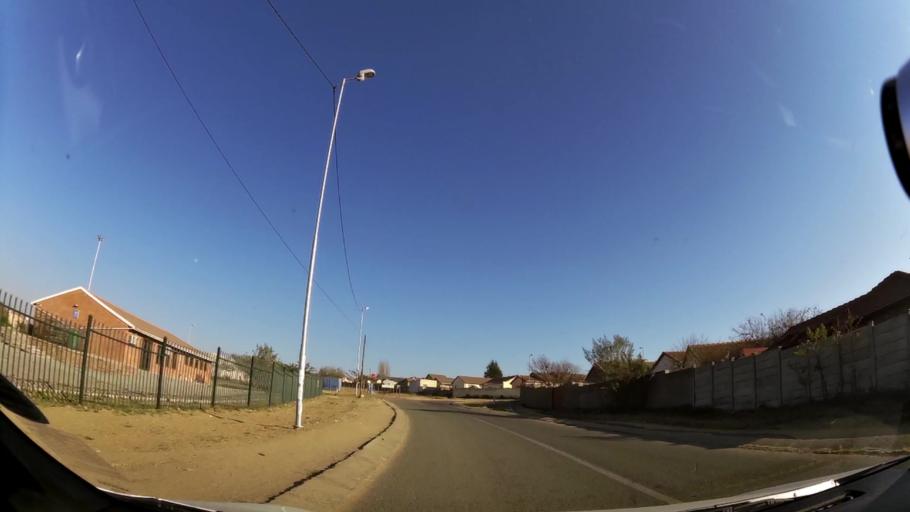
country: ZA
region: Gauteng
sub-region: City of Johannesburg Metropolitan Municipality
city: Midrand
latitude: -25.9129
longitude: 28.1041
